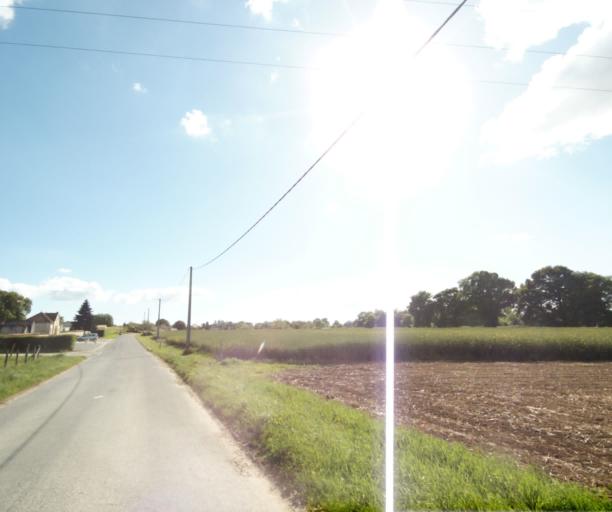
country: FR
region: Poitou-Charentes
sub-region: Departement de la Charente-Maritime
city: Nieul-les-Saintes
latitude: 45.7083
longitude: -0.7305
